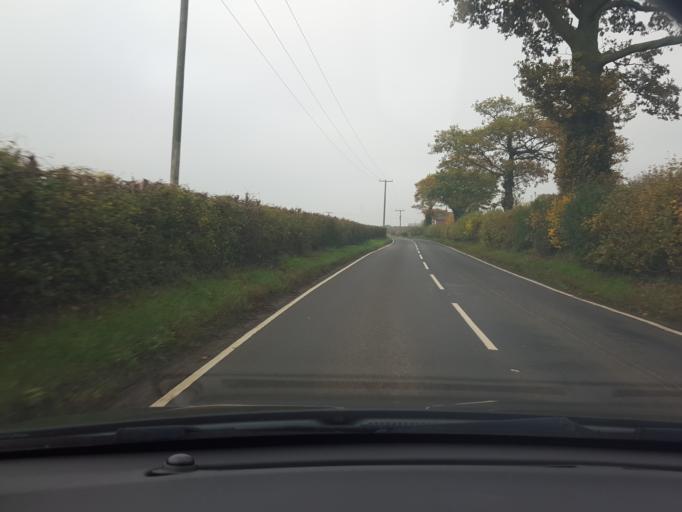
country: GB
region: England
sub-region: Essex
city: Alresford
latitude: 51.8983
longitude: 1.0168
